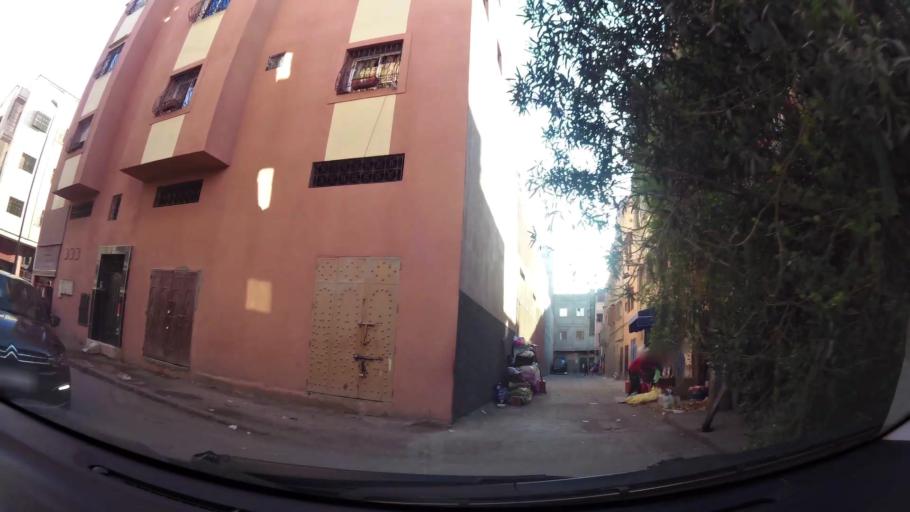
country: MA
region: Marrakech-Tensift-Al Haouz
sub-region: Marrakech
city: Marrakesh
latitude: 31.6195
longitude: -8.0597
